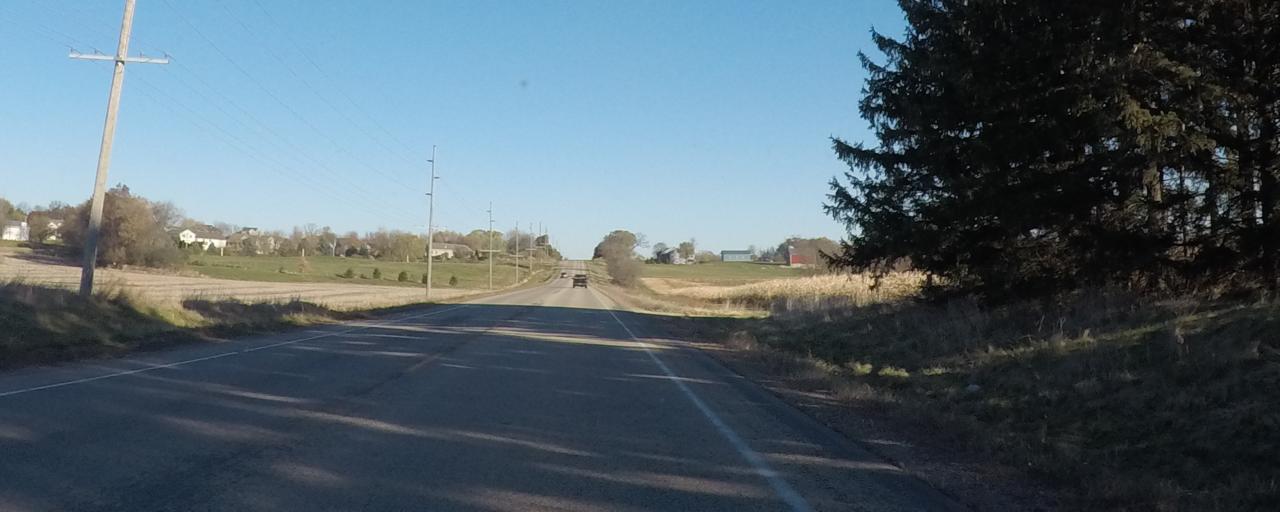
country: US
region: Wisconsin
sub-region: Dane County
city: Cottage Grove
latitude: 43.0446
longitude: -89.1999
